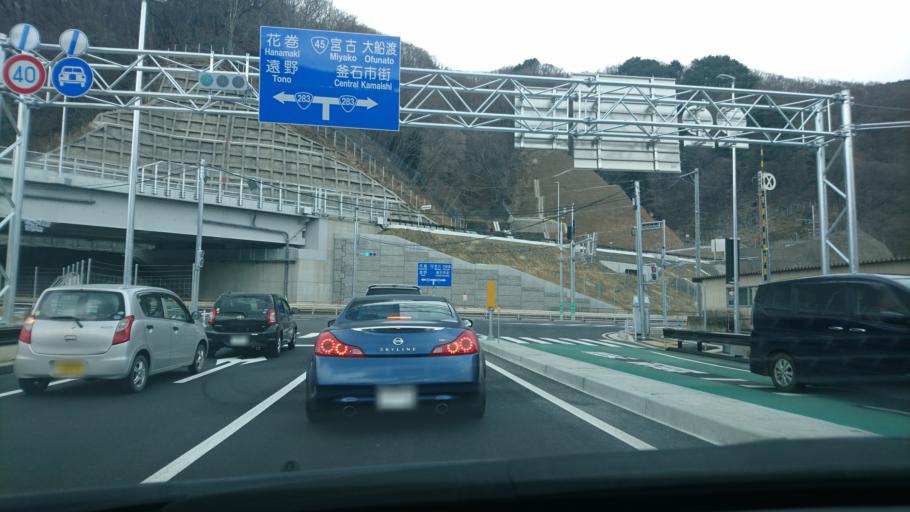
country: JP
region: Iwate
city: Kamaishi
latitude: 39.2657
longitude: 141.8450
